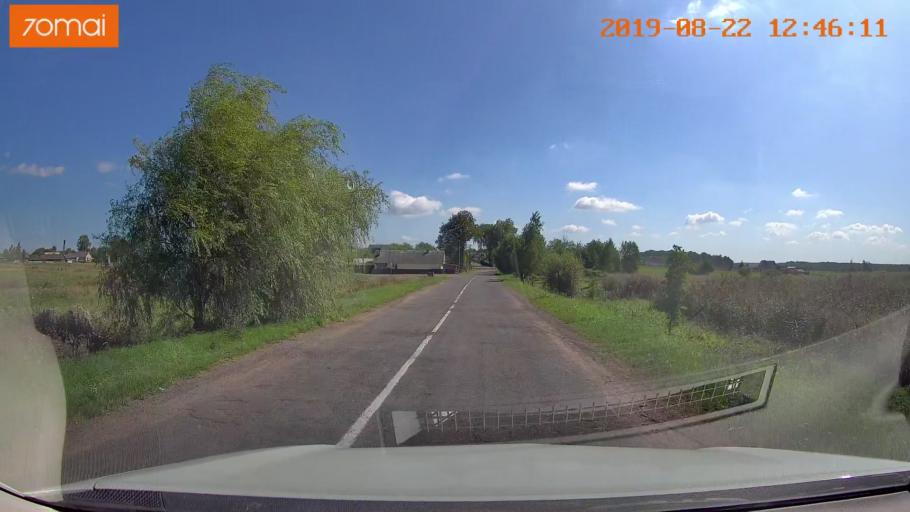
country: BY
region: Minsk
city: Prawdzinski
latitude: 53.4600
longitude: 27.6254
